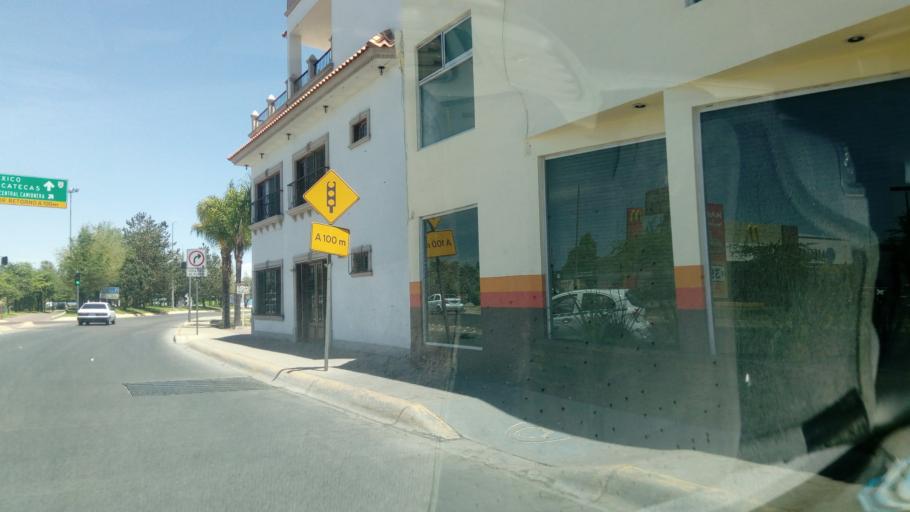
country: MX
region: Durango
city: Victoria de Durango
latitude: 24.0323
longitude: -104.6398
